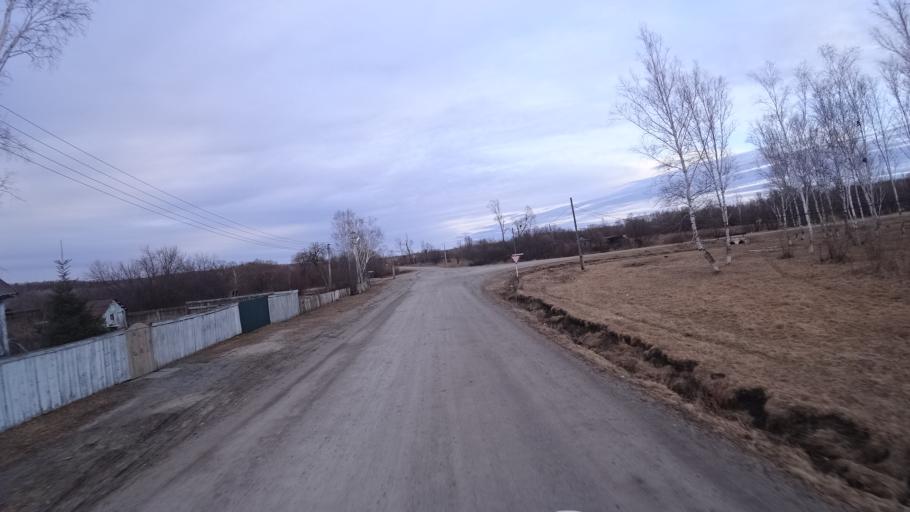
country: RU
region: Amur
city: Bureya
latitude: 50.0200
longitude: 129.7722
